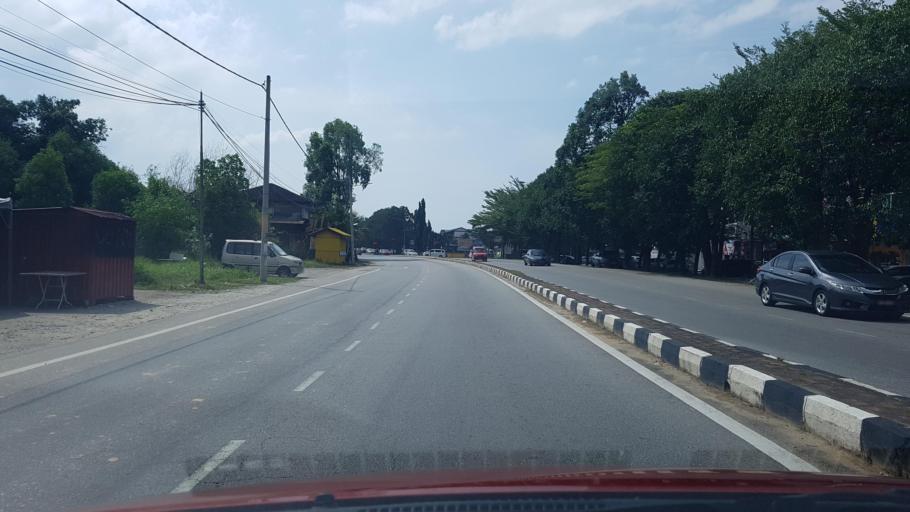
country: MY
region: Terengganu
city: Kuala Terengganu
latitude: 5.3563
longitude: 103.0948
